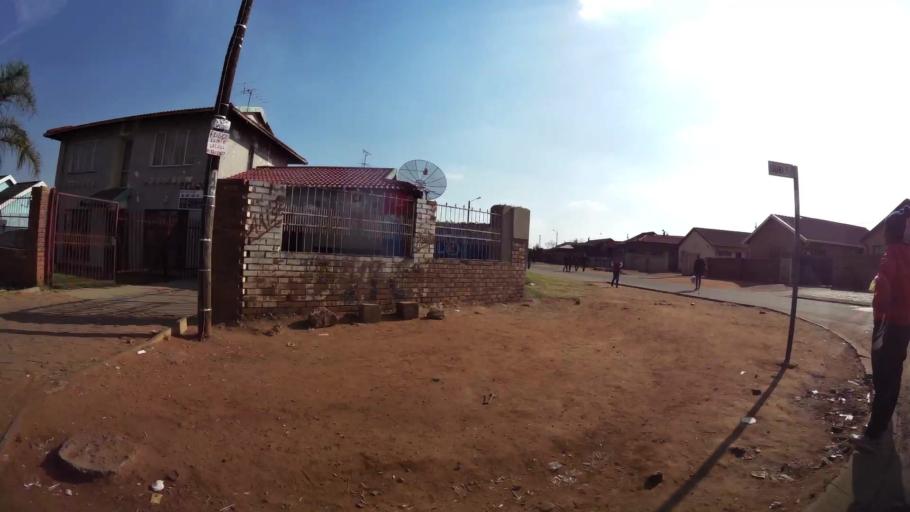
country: ZA
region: Gauteng
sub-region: Ekurhuleni Metropolitan Municipality
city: Benoni
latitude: -26.1495
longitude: 28.4019
